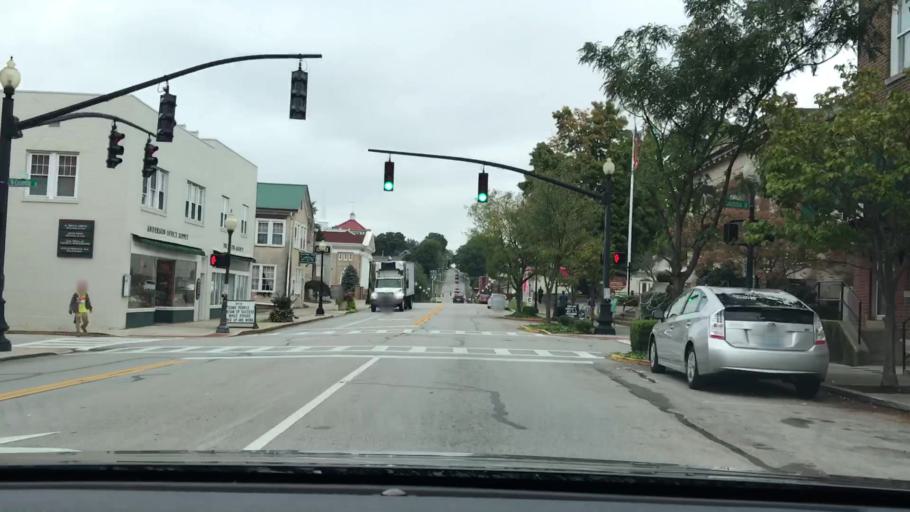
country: US
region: Kentucky
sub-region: Pulaski County
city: Somerset
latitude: 37.0926
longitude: -84.6048
